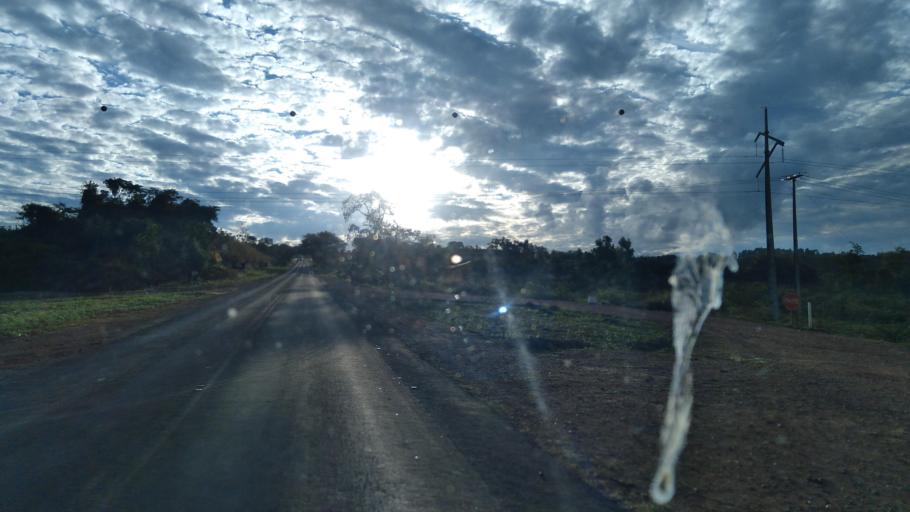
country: BR
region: Goias
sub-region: Mineiros
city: Mineiros
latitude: -17.5805
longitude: -52.5273
